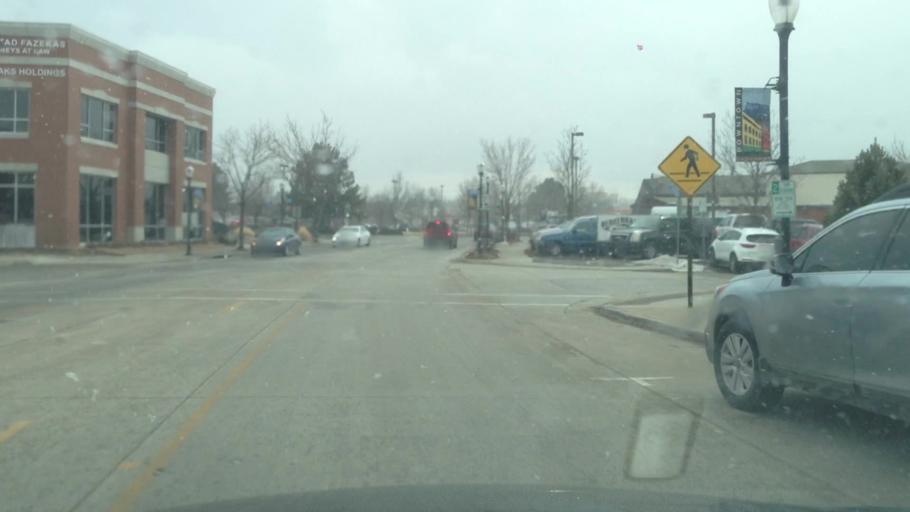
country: US
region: Colorado
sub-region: Douglas County
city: Castle Rock
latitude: 39.3694
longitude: -104.8601
